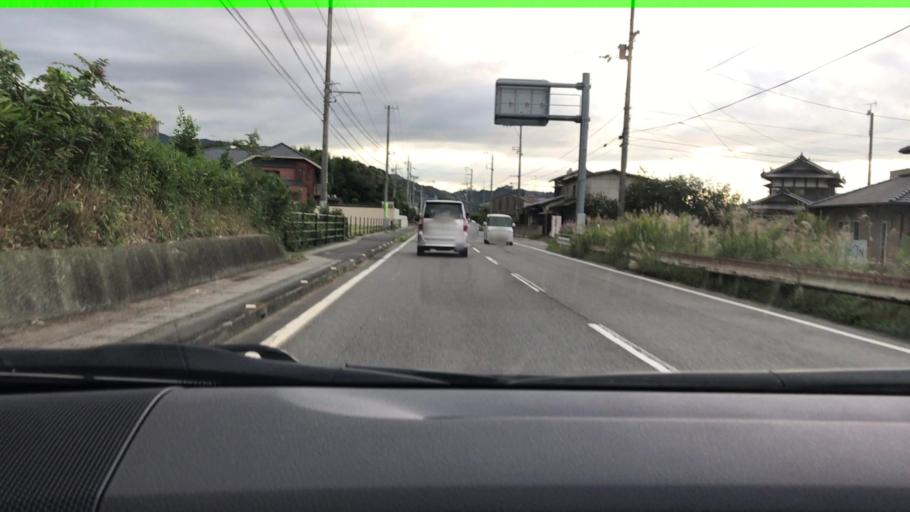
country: JP
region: Ehime
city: Hojo
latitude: 34.0657
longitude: 132.9337
